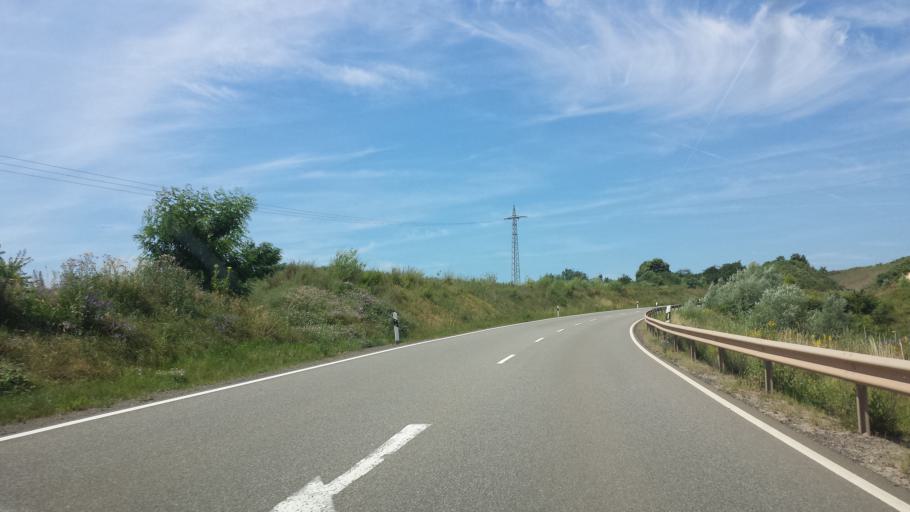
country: DE
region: Rheinland-Pfalz
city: Eisenberg
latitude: 49.5657
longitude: 8.0805
